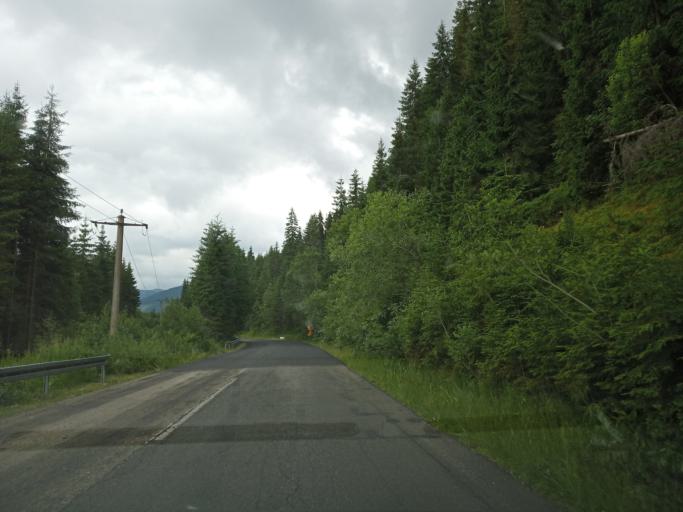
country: RO
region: Gorj
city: Novaci-Straini
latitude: 45.4246
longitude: 23.6901
